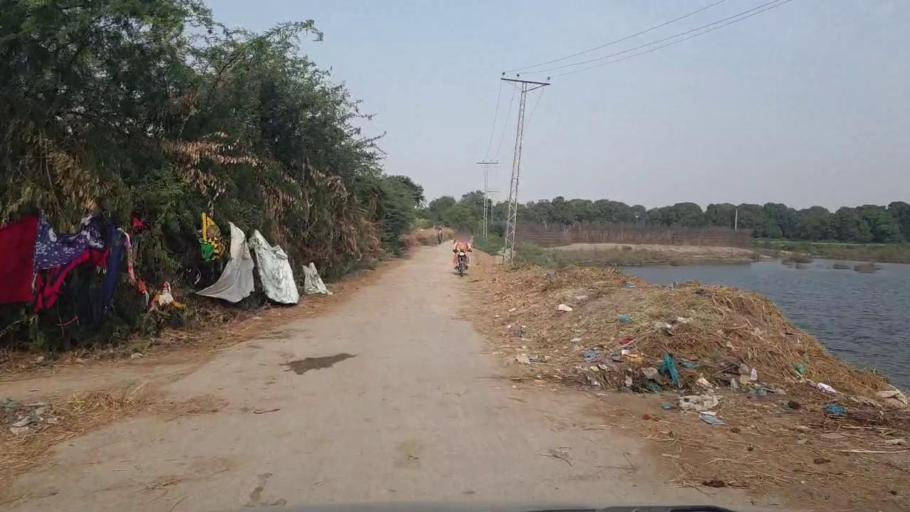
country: PK
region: Sindh
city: Tando Muhammad Khan
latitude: 25.1129
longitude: 68.3679
